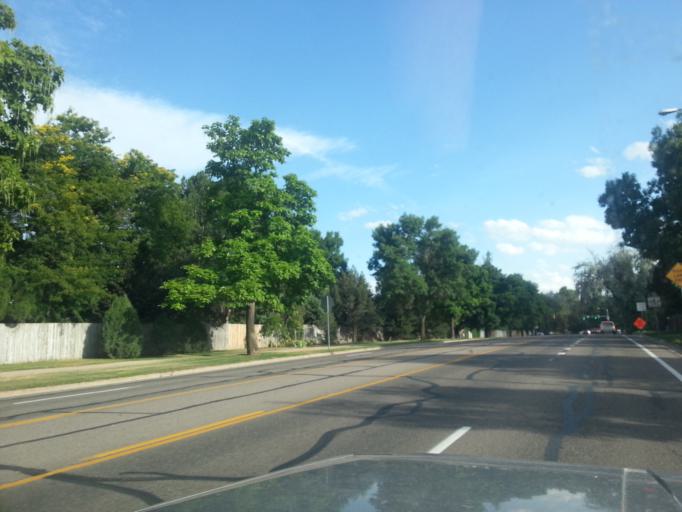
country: US
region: Colorado
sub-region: Larimer County
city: Fort Collins
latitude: 40.5400
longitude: -105.0580
